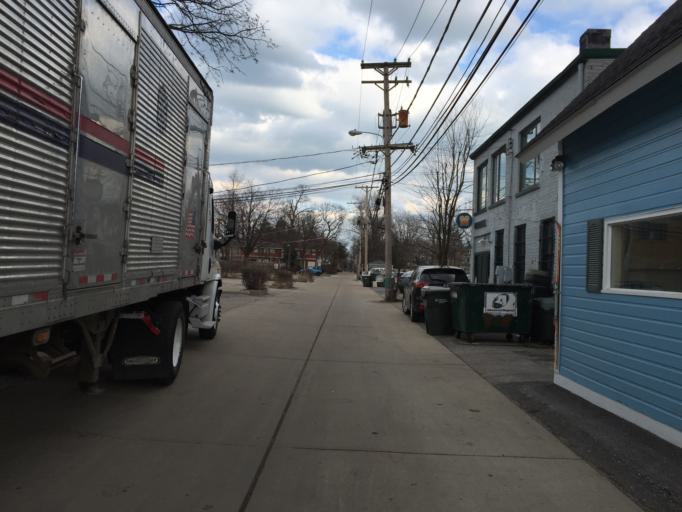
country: US
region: Illinois
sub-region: Cook County
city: Kenilworth
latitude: 42.0760
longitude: -87.7064
